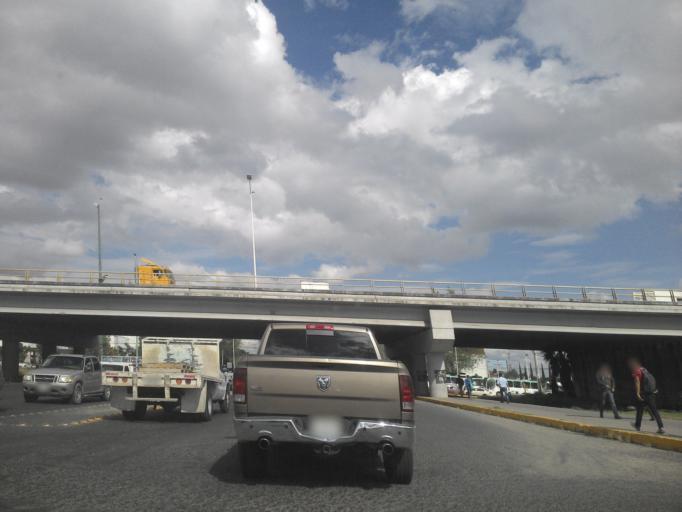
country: MX
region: Jalisco
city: Guadalajara
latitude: 20.6584
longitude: -103.4481
